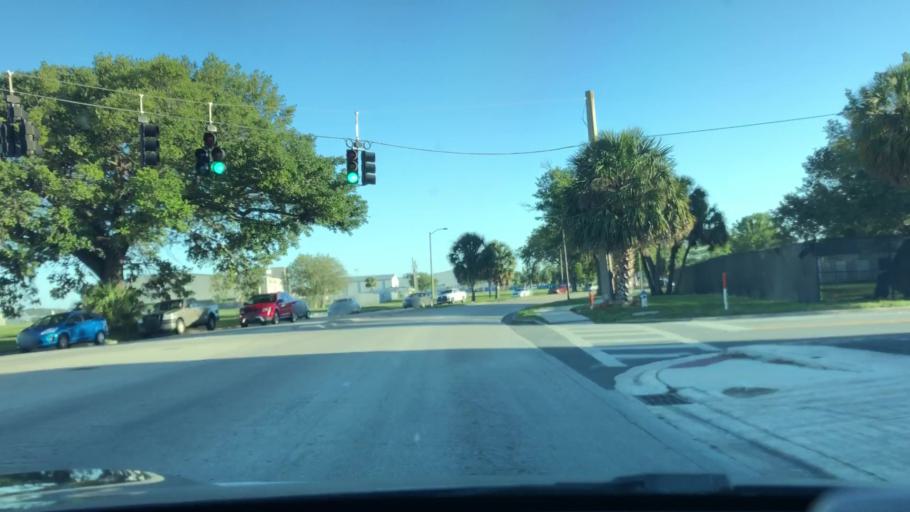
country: US
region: Florida
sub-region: Orange County
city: Orlando
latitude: 28.5517
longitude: -81.3448
